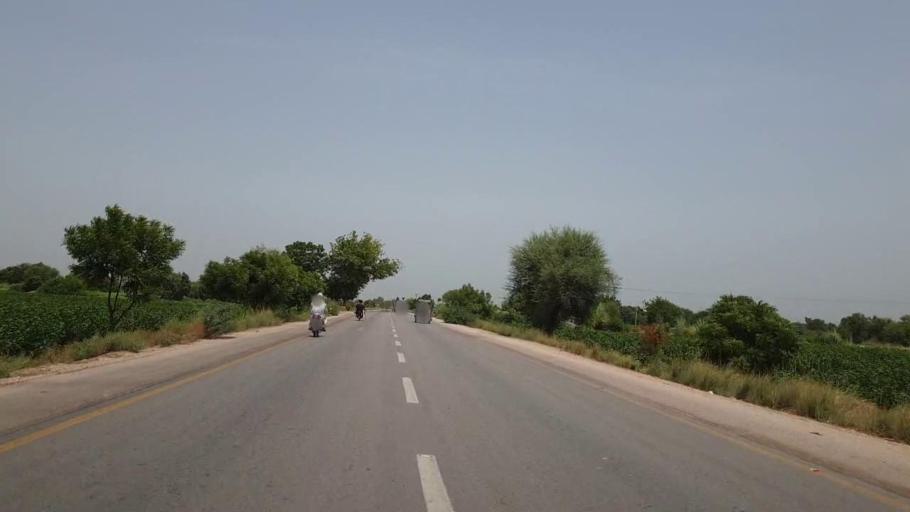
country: PK
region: Sindh
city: Nawabshah
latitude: 26.2434
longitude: 68.4665
